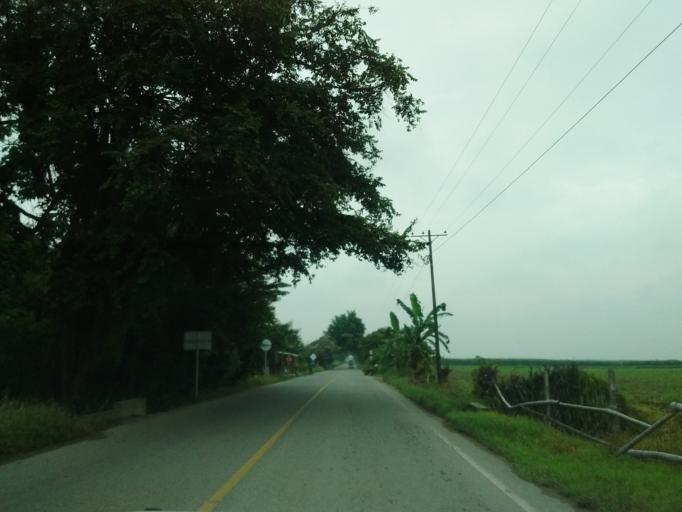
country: CO
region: Cauca
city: Padilla
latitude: 3.2251
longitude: -76.3578
